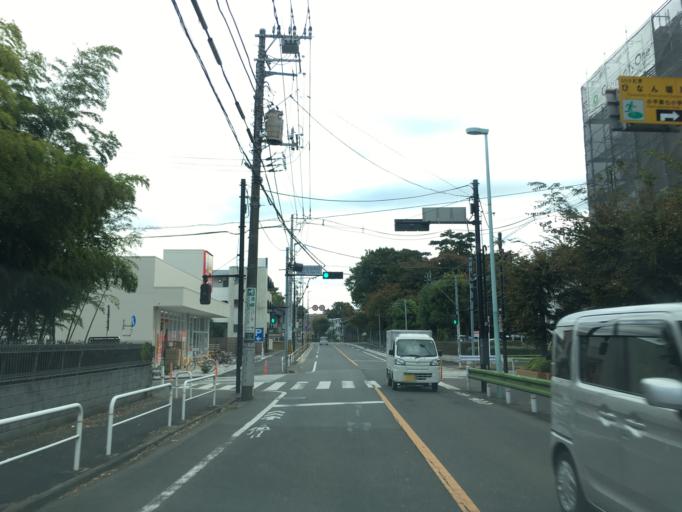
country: JP
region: Tokyo
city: Higashimurayama-shi
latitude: 35.7377
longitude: 139.4959
